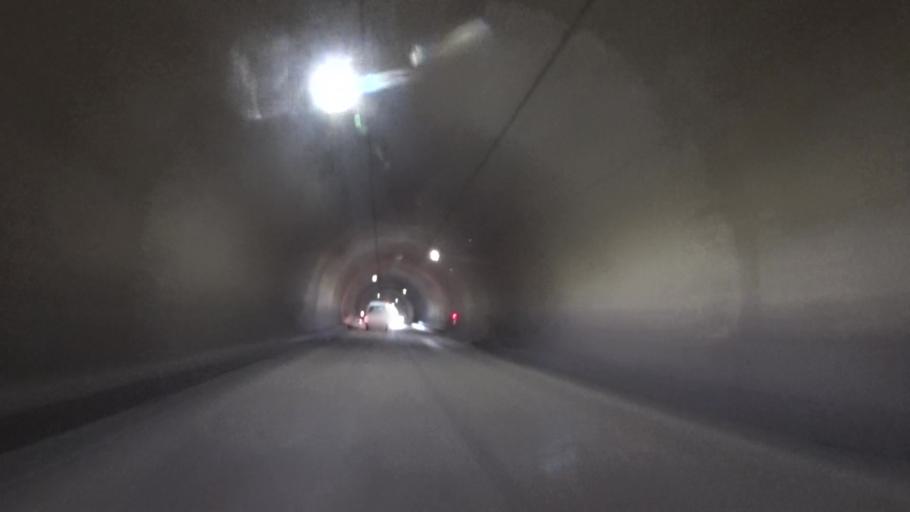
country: JP
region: Kyoto
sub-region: Kyoto-shi
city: Kamigyo-ku
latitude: 35.1000
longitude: 135.7652
